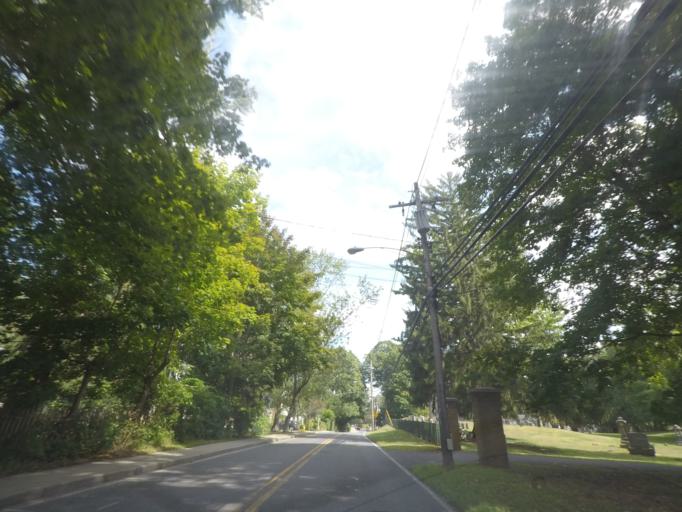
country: US
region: New York
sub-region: Albany County
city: Delmar
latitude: 42.6216
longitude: -73.8225
